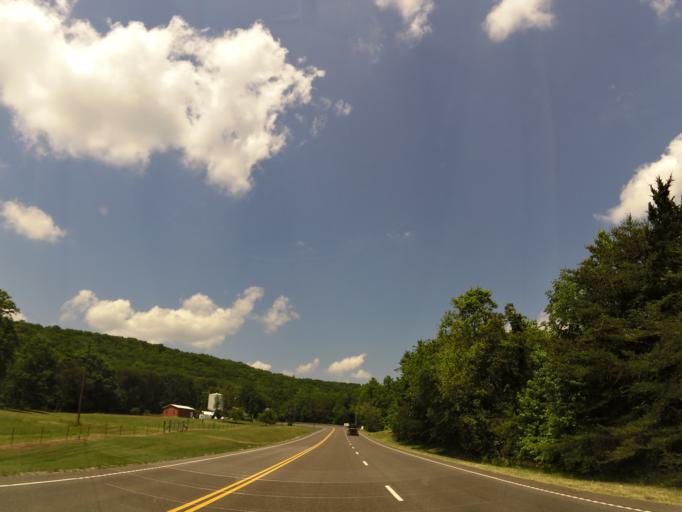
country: US
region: Tennessee
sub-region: Rhea County
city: Dayton
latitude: 35.5210
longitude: -85.0407
